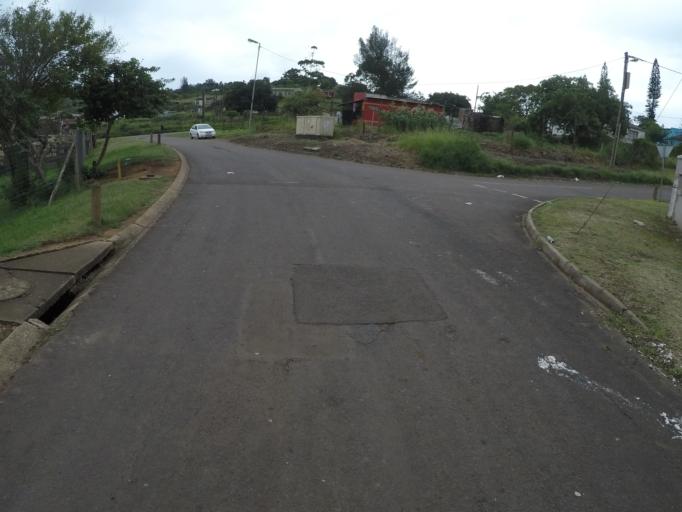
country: ZA
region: KwaZulu-Natal
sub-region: uThungulu District Municipality
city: Empangeni
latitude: -28.7734
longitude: 31.8541
